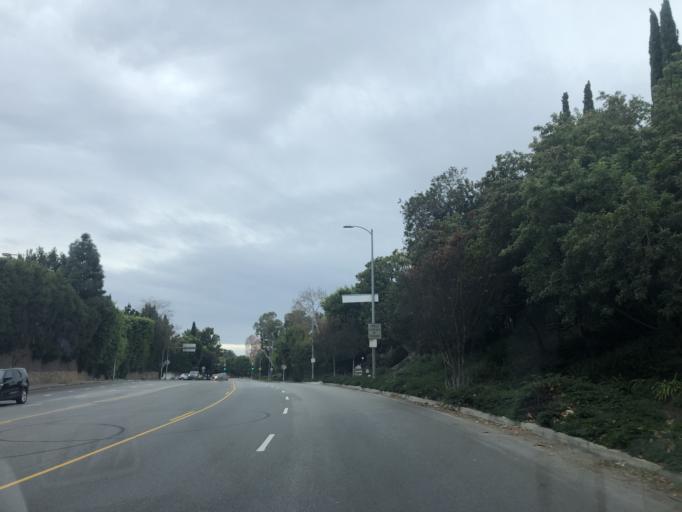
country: US
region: California
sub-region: Los Angeles County
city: Westwood, Los Angeles
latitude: 34.0719
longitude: -118.4684
